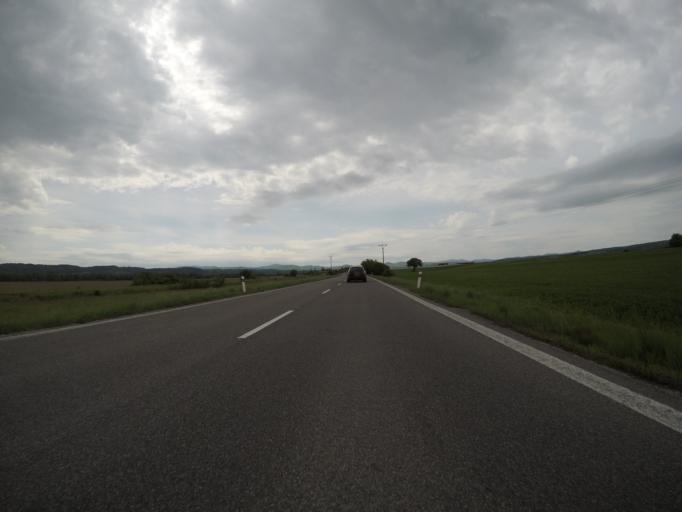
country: SK
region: Banskobystricky
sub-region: Okres Banska Bystrica
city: Zvolen
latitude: 48.6498
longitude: 19.1426
